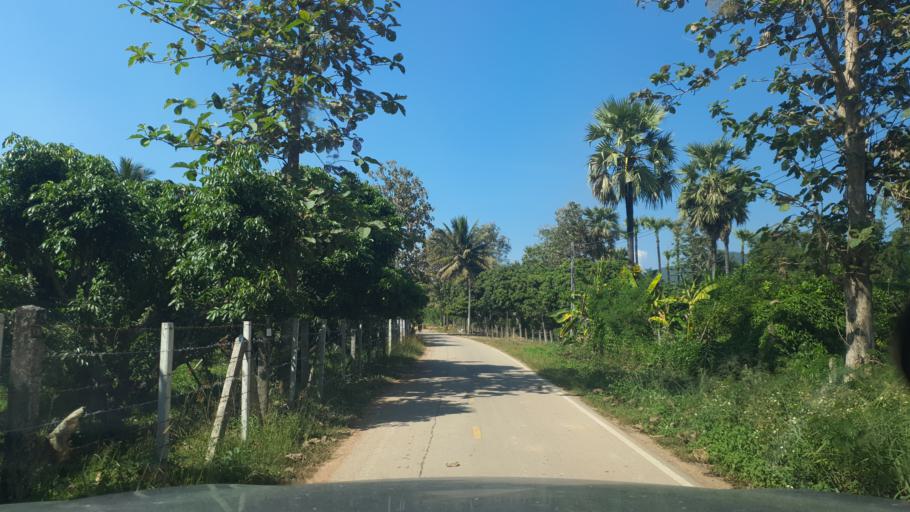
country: TH
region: Chiang Mai
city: Mae On
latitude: 18.7251
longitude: 99.2171
